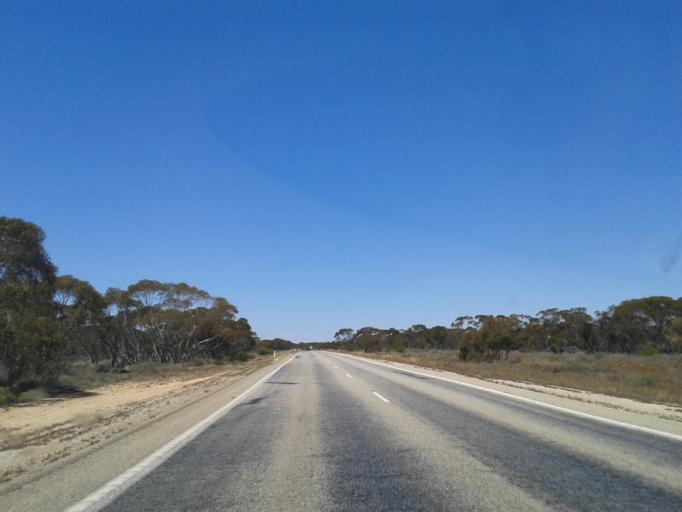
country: AU
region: New South Wales
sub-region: Wentworth
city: Gol Gol
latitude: -34.4248
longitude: 142.4528
